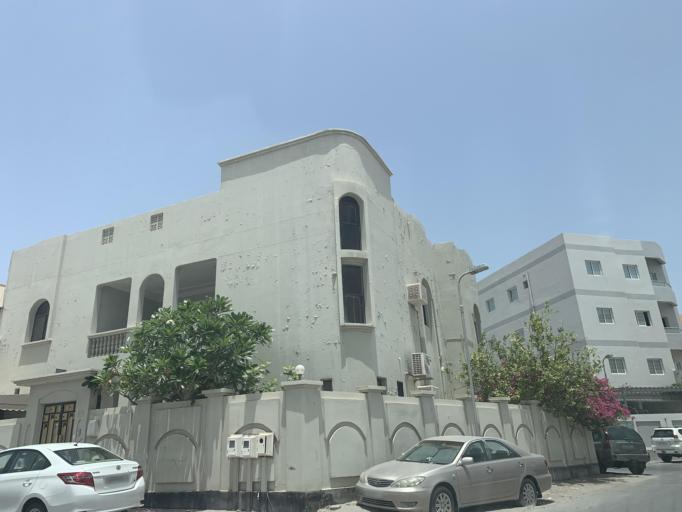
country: BH
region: Northern
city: Madinat `Isa
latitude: 26.1699
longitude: 50.5701
